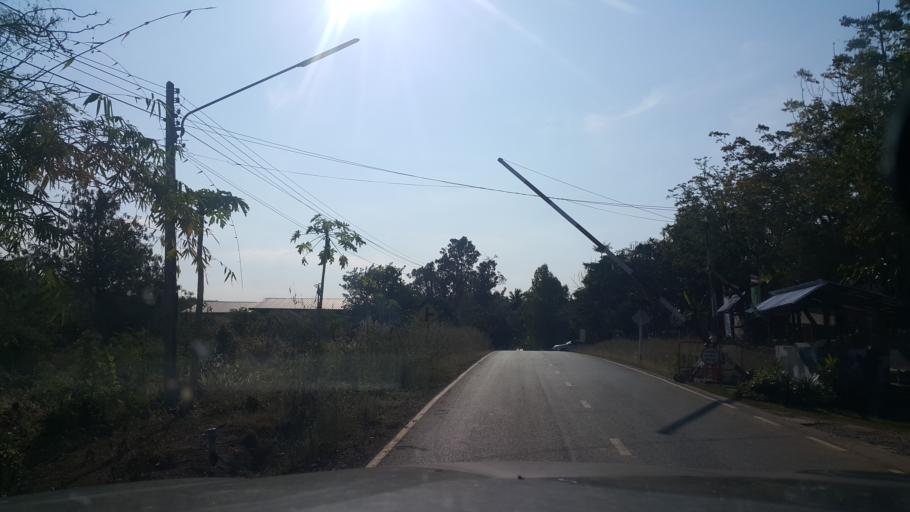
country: TH
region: Loei
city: Chiang Khan
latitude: 17.8055
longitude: 101.6222
